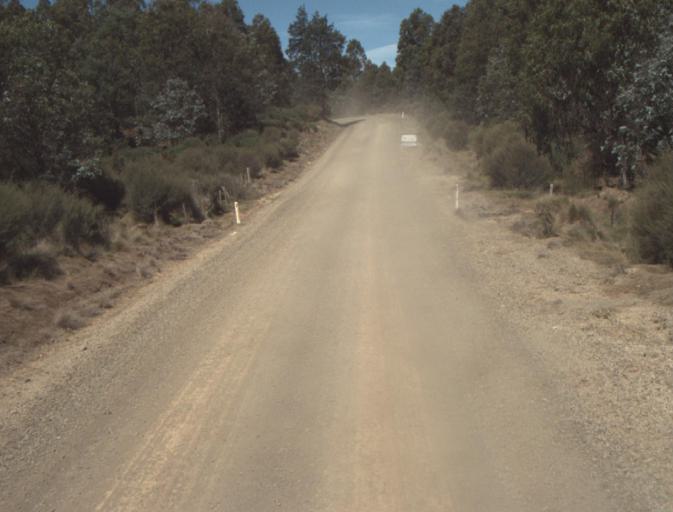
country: AU
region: Tasmania
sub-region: Dorset
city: Scottsdale
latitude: -41.3234
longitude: 147.4656
